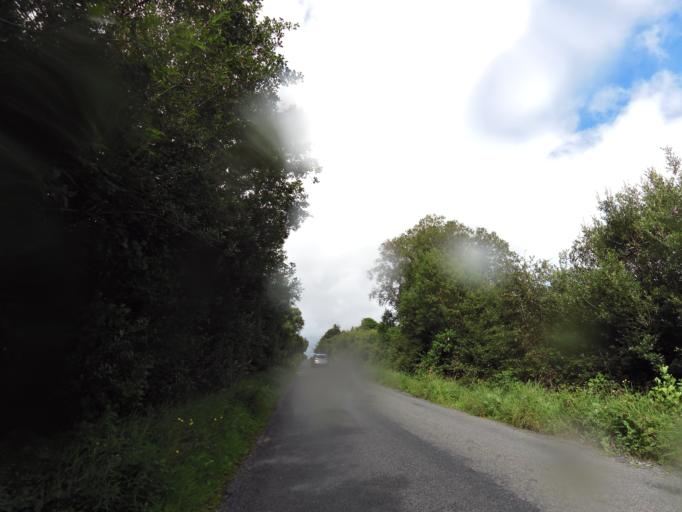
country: IE
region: Connaught
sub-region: County Galway
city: Oughterard
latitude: 53.4167
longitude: -9.3301
